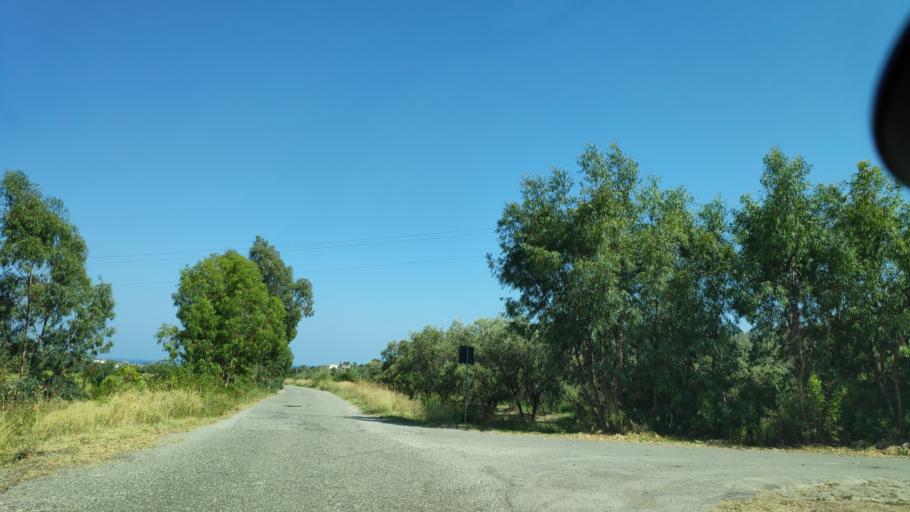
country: IT
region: Calabria
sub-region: Provincia di Reggio Calabria
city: Riace Marina
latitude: 38.4282
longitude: 16.5236
